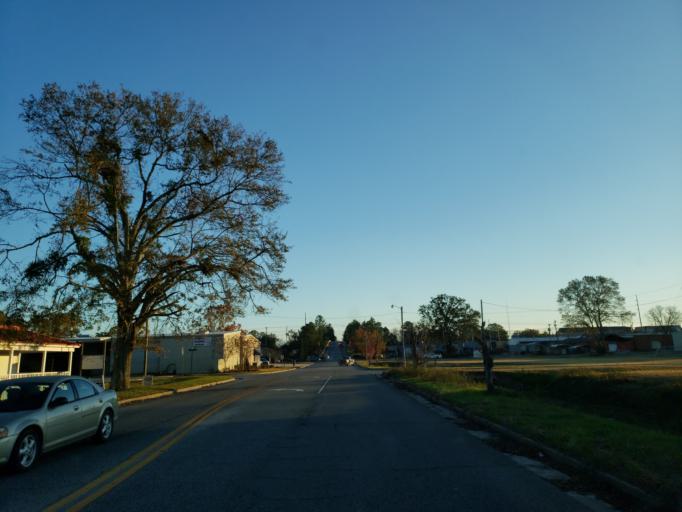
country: US
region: Georgia
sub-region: Crisp County
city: Cordele
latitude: 31.9735
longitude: -83.7797
